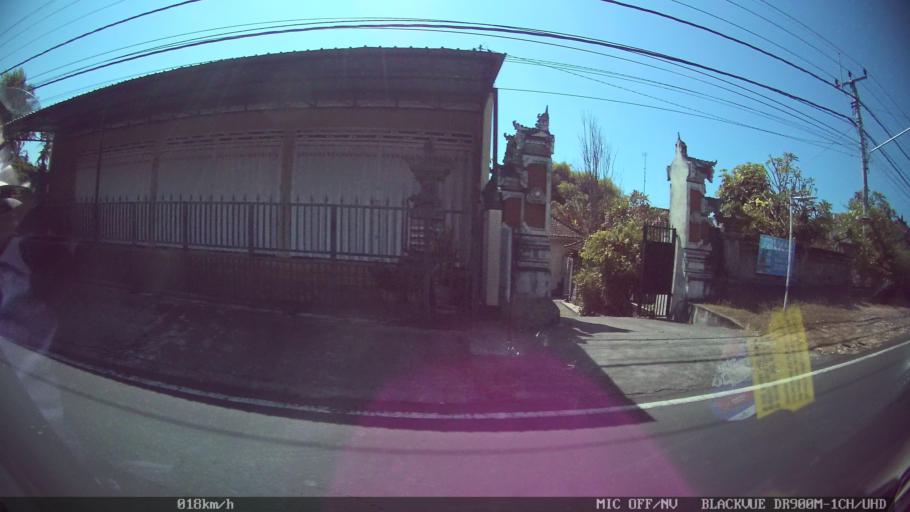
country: ID
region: Bali
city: Banjar Banyualit
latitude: -8.1531
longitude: 115.0401
